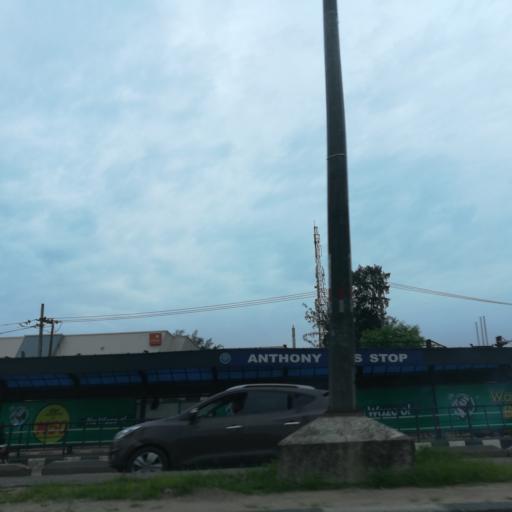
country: NG
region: Lagos
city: Somolu
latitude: 6.5573
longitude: 3.3666
